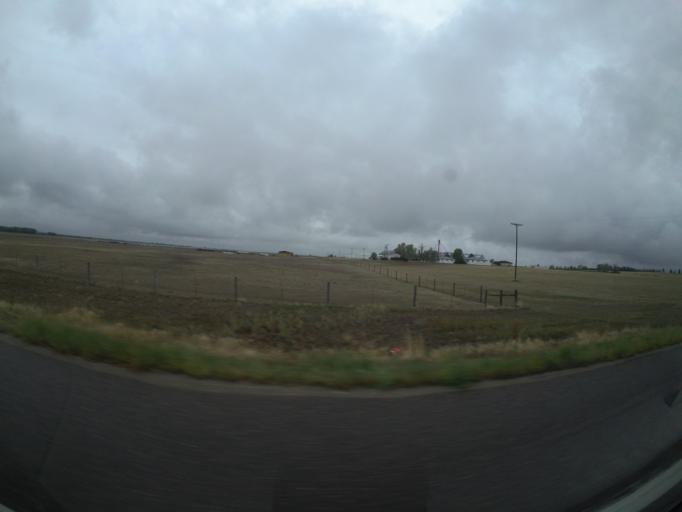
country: US
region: Colorado
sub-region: Arapahoe County
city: Byers
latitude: 39.7400
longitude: -104.1131
